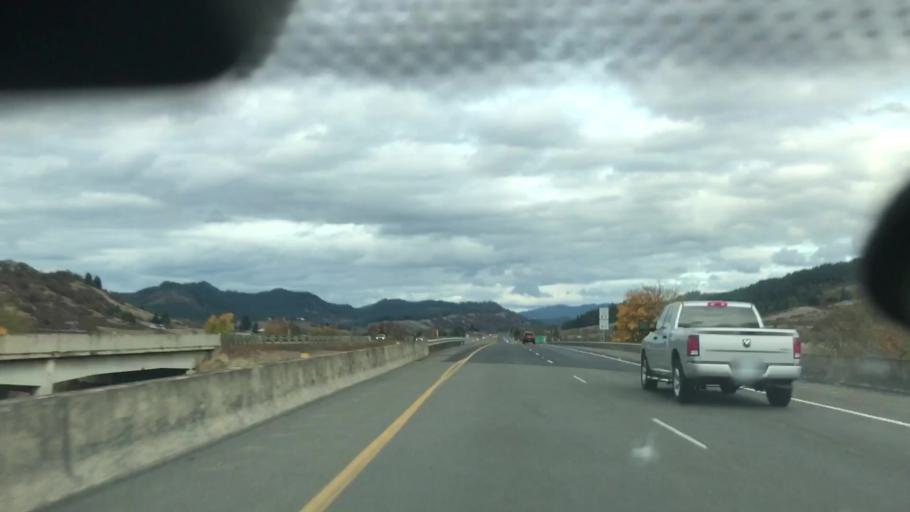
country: US
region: Oregon
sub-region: Douglas County
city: Yoncalla
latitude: 43.5688
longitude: -123.2738
